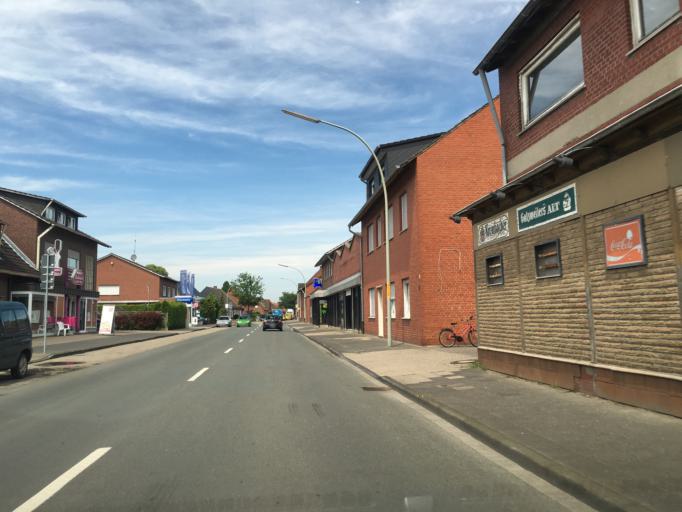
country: DE
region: North Rhine-Westphalia
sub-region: Regierungsbezirk Munster
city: Nordwalde
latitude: 52.0897
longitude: 7.4814
